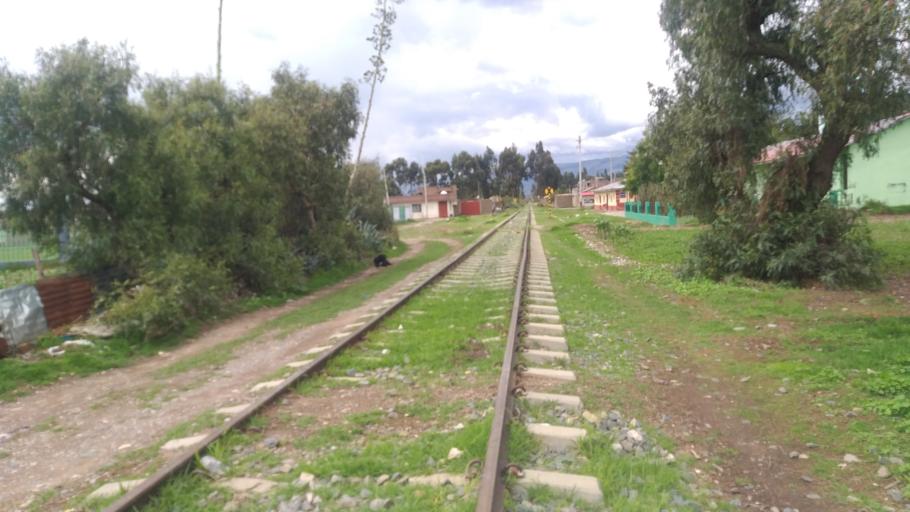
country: PE
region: Junin
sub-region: Provincia de Huancayo
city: Huayucachi
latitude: -12.1222
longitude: -75.2243
